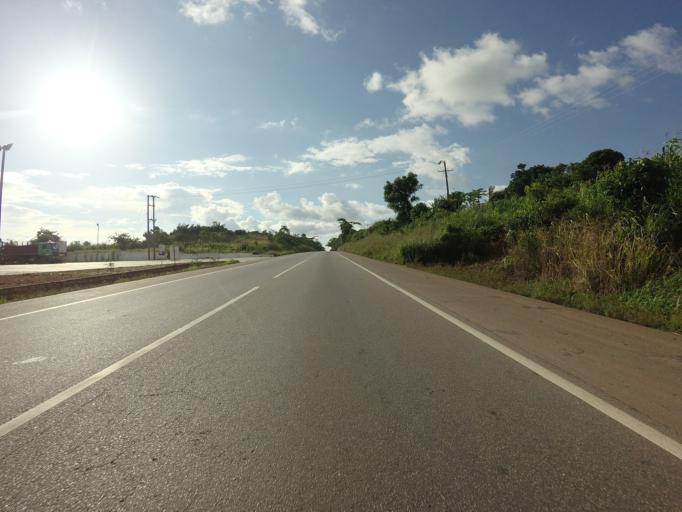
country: GH
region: Ashanti
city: Tafo
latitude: 6.8875
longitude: -1.6465
